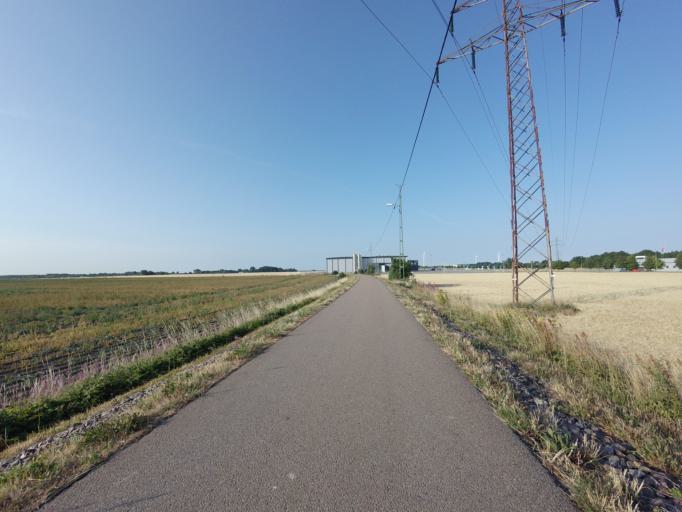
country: SE
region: Skane
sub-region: Landskrona
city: Asmundtorp
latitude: 55.8741
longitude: 12.8897
